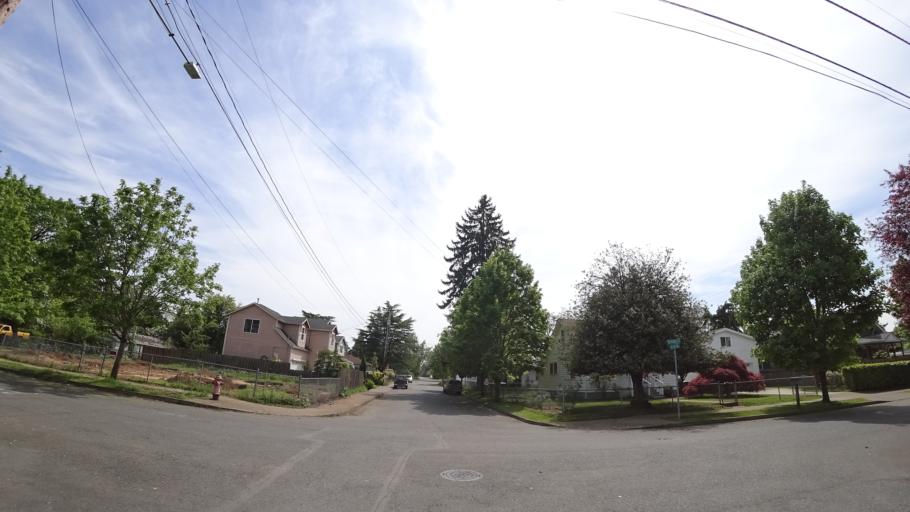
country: US
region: Oregon
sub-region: Multnomah County
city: Lents
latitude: 45.4727
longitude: -122.6074
